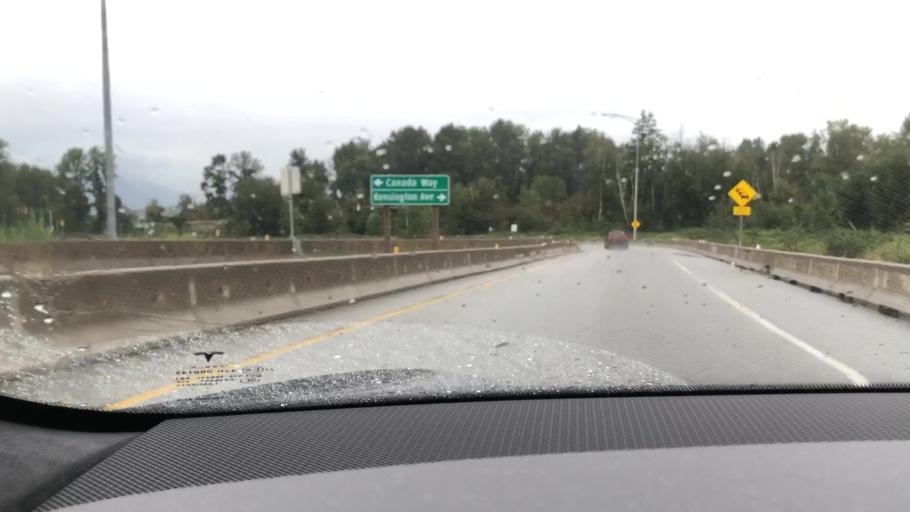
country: CA
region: British Columbia
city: Burnaby
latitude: 49.2441
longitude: -122.9640
